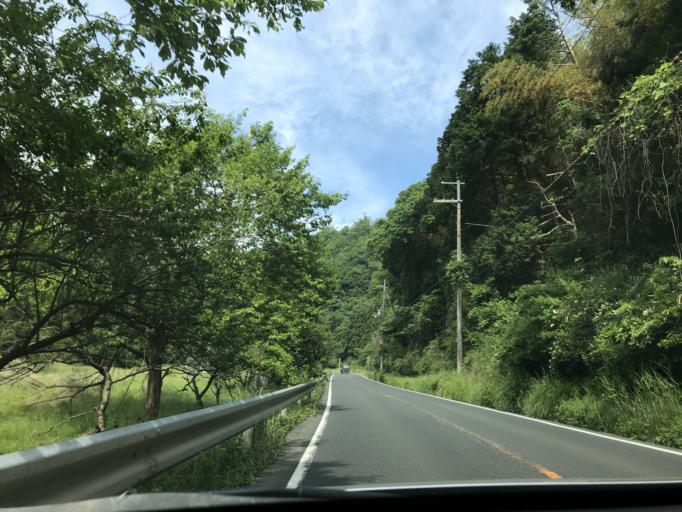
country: JP
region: Kyoto
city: Miyazu
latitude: 35.6632
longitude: 135.0151
